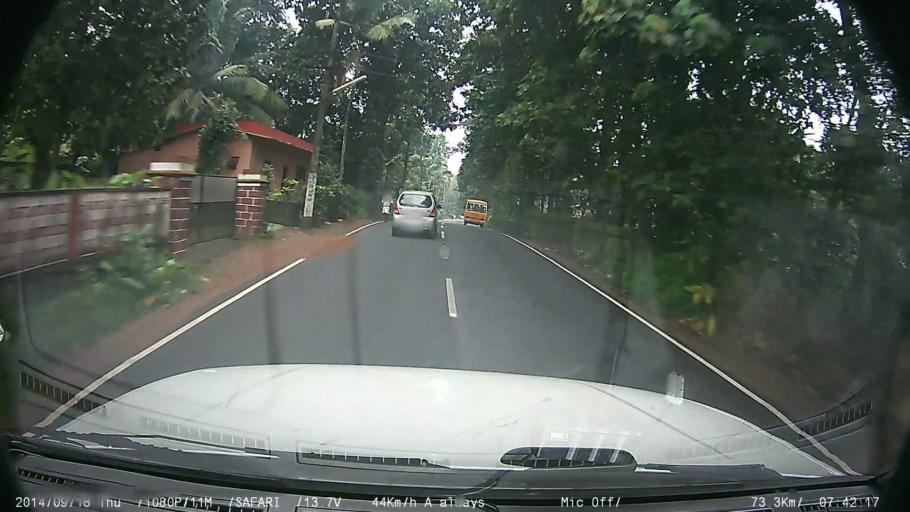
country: IN
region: Kerala
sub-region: Kottayam
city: Changanacheri
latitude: 9.4653
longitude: 76.5787
